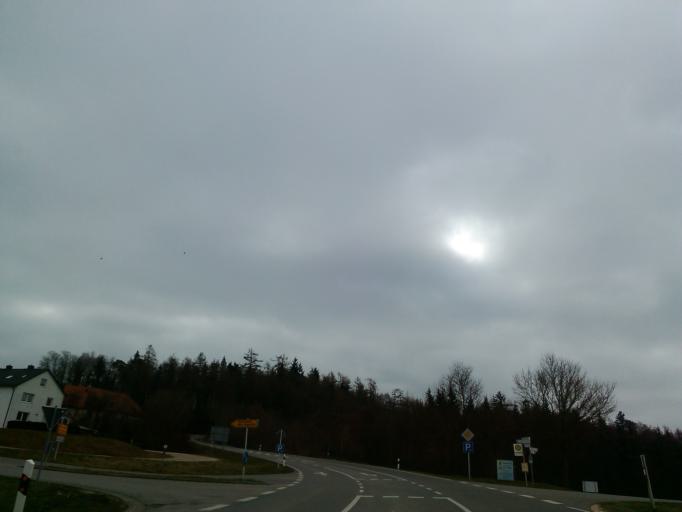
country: DE
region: Bavaria
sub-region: Swabia
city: Ziemetshausen
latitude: 48.2802
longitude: 10.5403
